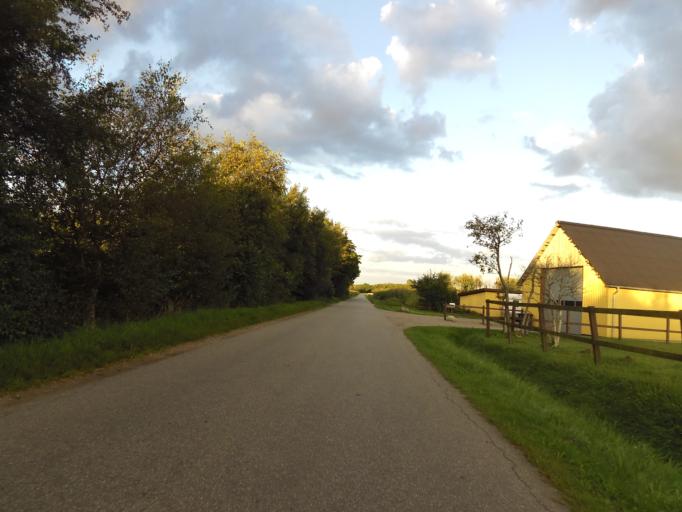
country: DK
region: South Denmark
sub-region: Tonder Kommune
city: Sherrebek
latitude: 55.2407
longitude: 8.8613
